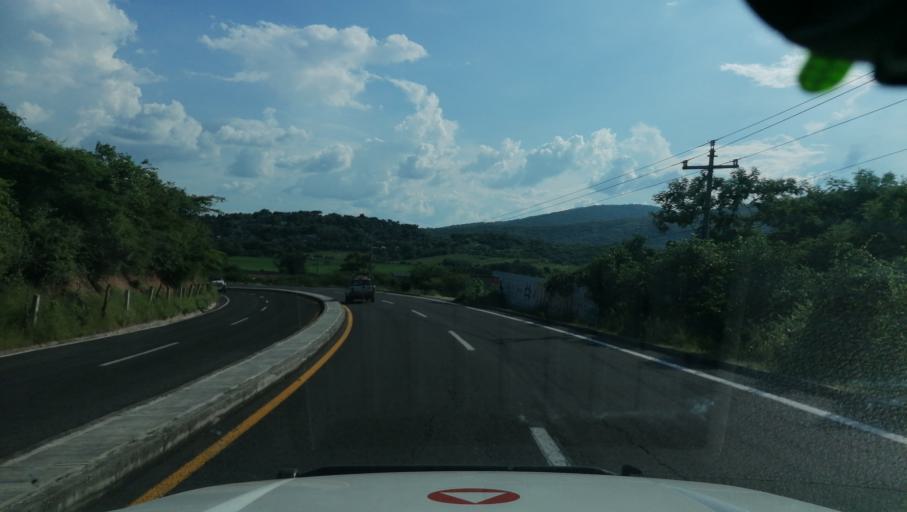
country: MX
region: Morelos
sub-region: Ayala
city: Abelardo L. Rodriguez
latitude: 18.7003
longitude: -98.9937
